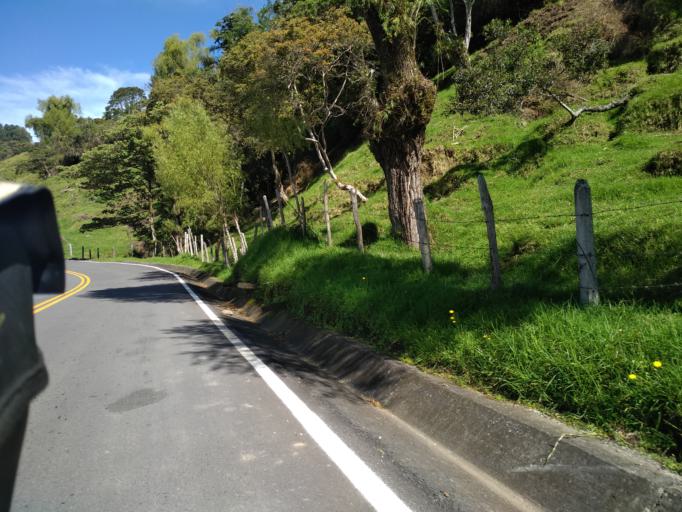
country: CO
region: Santander
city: Velez
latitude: 6.0017
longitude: -73.6963
